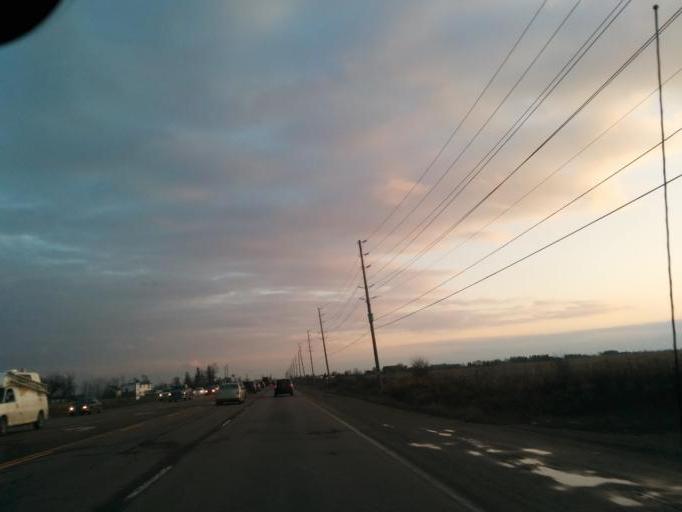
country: CA
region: Ontario
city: Brampton
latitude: 43.8462
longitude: -79.6943
